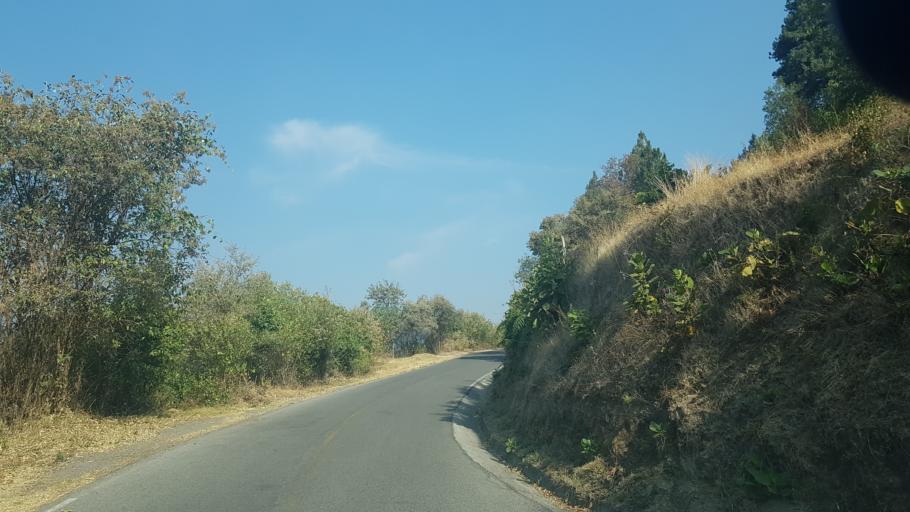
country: MX
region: Puebla
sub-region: Tochimilco
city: Santa Cruz Cuautomatitla
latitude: 18.8912
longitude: -98.6708
